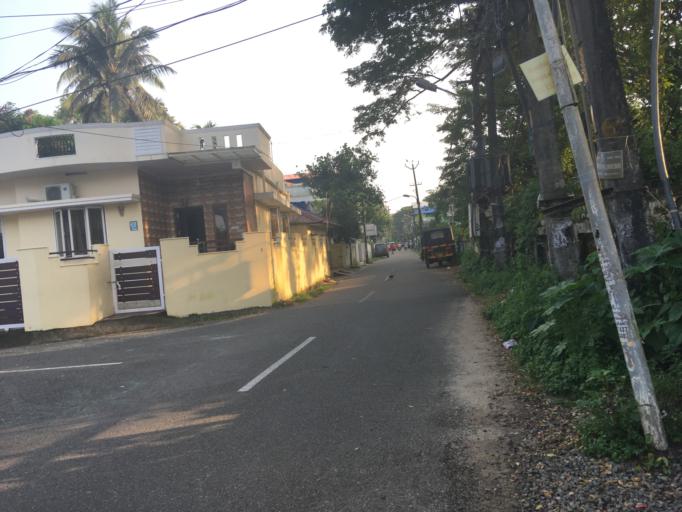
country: IN
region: Kerala
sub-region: Ernakulam
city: Cochin
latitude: 9.9575
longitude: 76.2405
